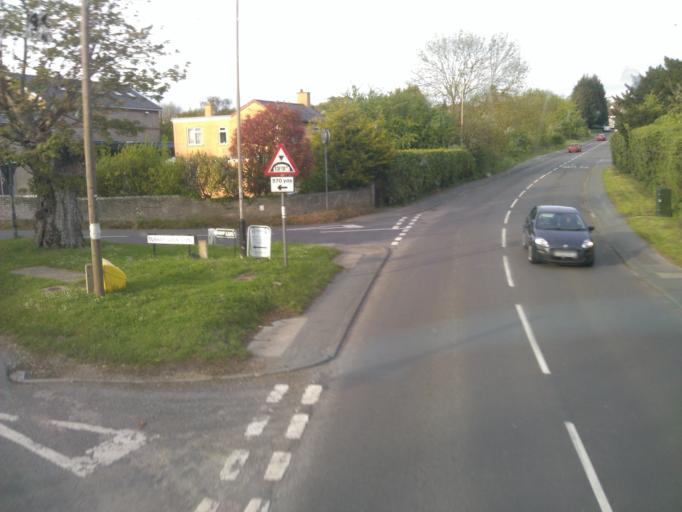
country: GB
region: England
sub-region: Essex
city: Eight Ash Green
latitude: 51.8826
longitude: 0.8103
